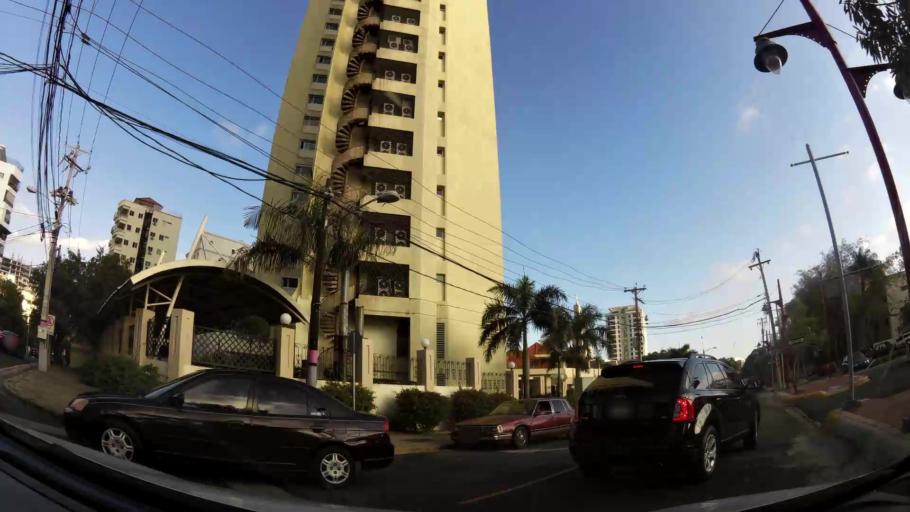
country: DO
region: Nacional
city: La Julia
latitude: 18.4683
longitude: -69.9178
